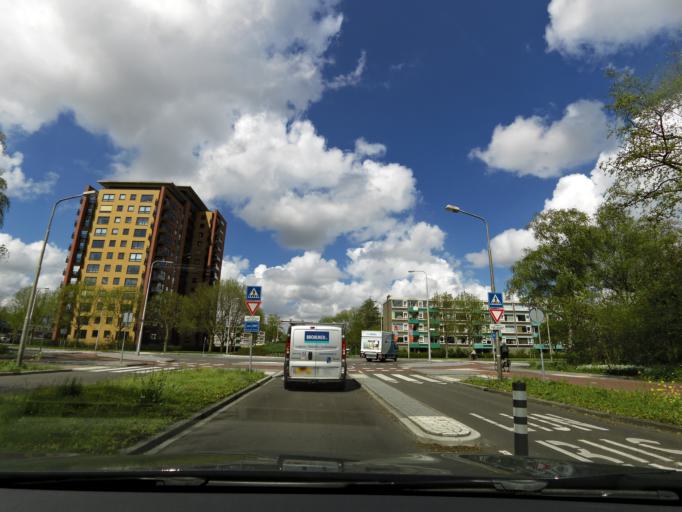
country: NL
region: North Holland
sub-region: Gemeente Amstelveen
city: Amstelveen
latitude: 52.2906
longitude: 4.8542
